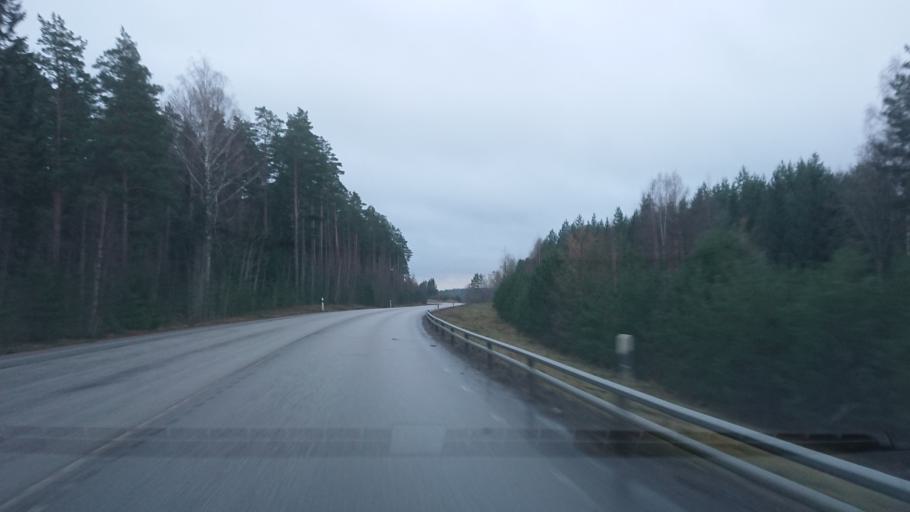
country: SE
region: Uppsala
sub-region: Osthammars Kommun
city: Bjorklinge
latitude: 60.0164
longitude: 17.5857
